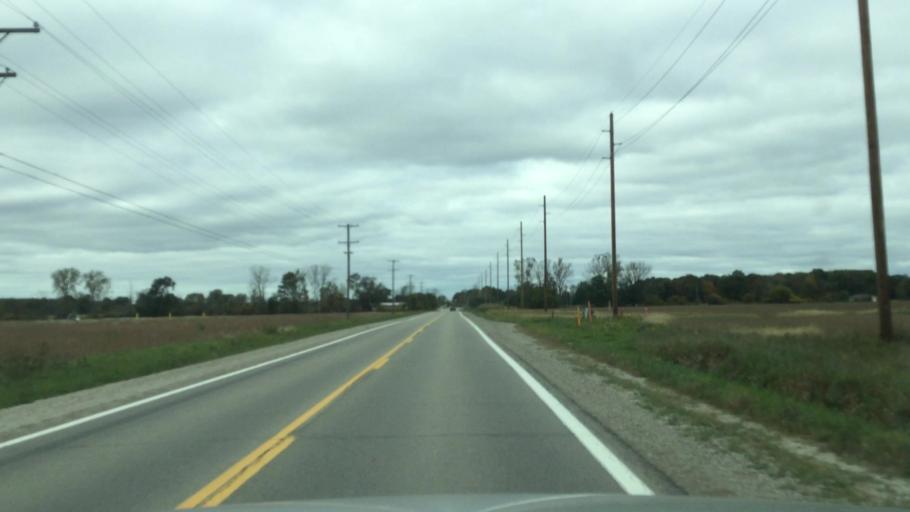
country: US
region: Michigan
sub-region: Macomb County
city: Armada
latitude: 42.8065
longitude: -82.8747
